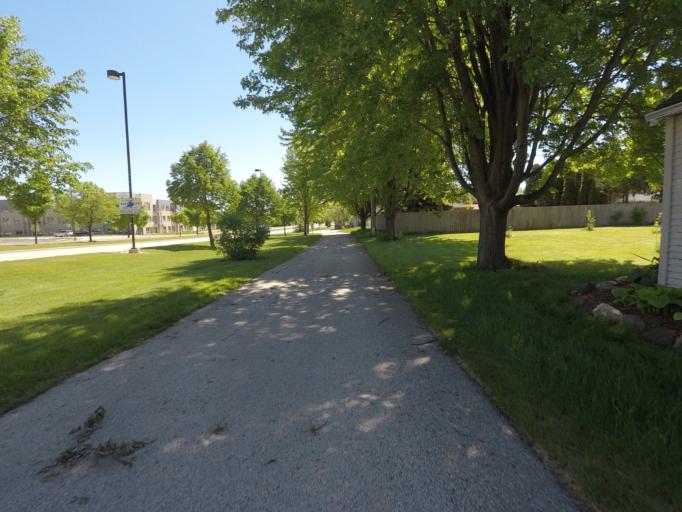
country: US
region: Wisconsin
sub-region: Sheboygan County
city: Sheboygan
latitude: 43.7562
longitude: -87.7444
